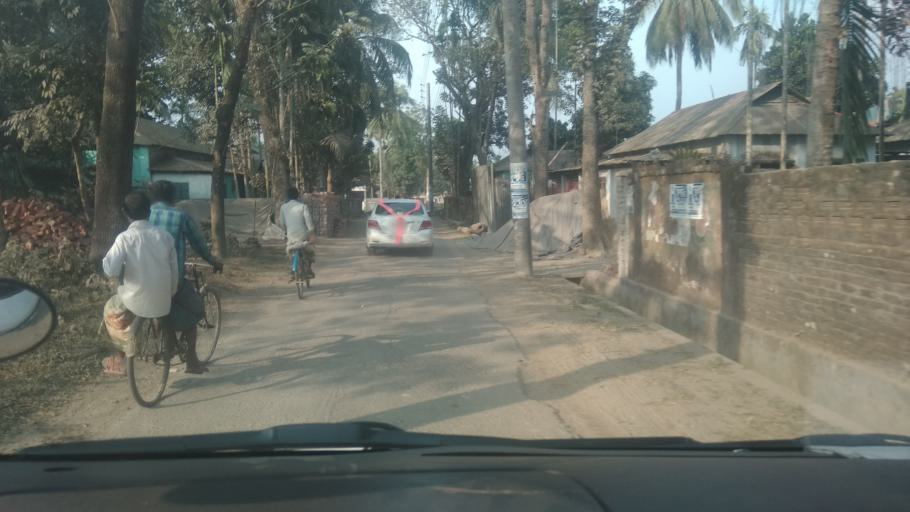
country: BD
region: Dhaka
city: Mymensingh
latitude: 24.7574
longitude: 90.5661
